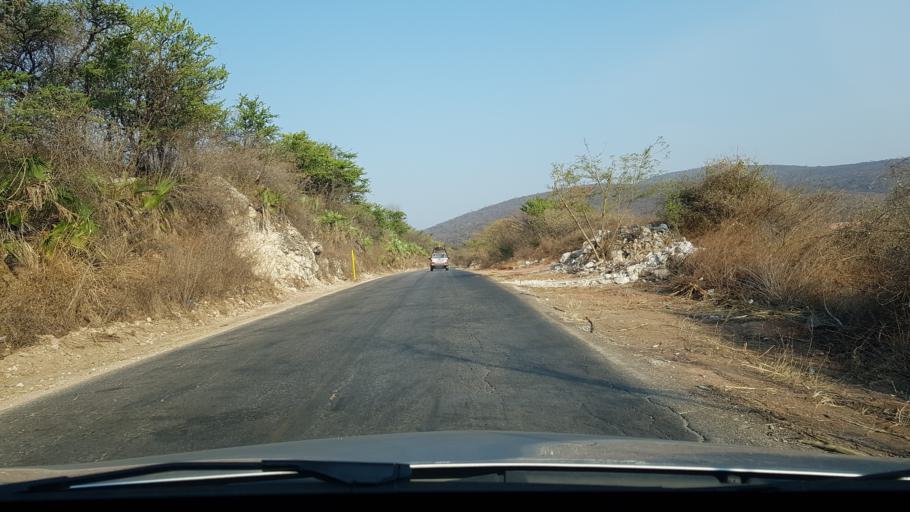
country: MX
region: Morelos
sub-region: Tlaltizapan de Zapata
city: Colonia Palo Prieto (Chipitongo)
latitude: 18.6732
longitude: -99.0589
